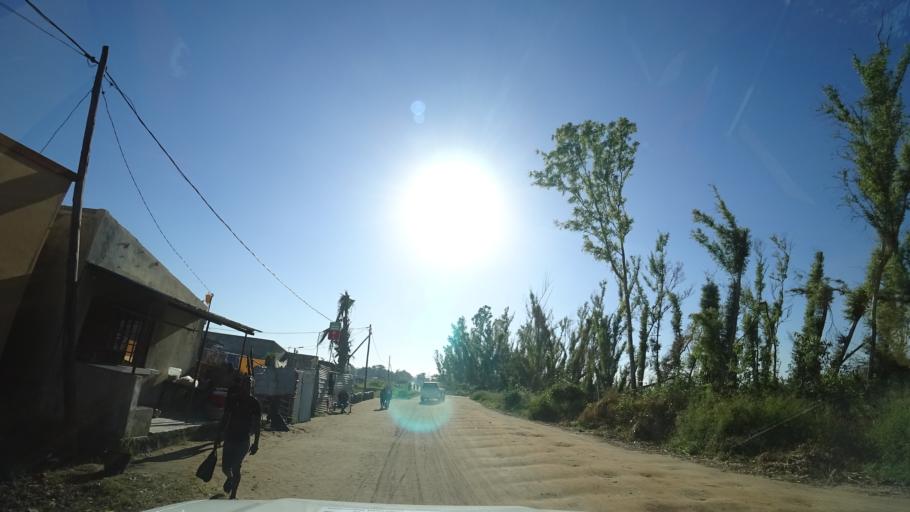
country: MZ
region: Sofala
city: Beira
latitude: -19.7696
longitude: 34.8896
